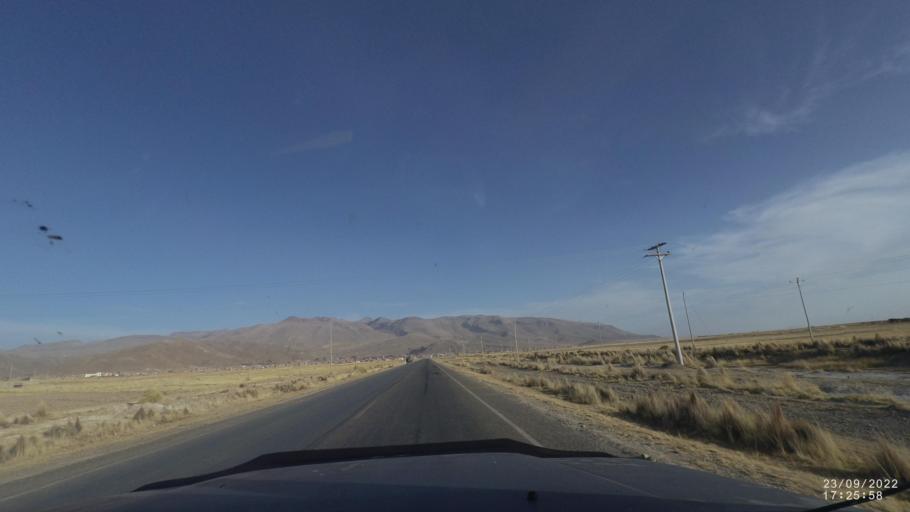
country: BO
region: Oruro
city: Challapata
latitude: -18.8783
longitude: -66.7912
